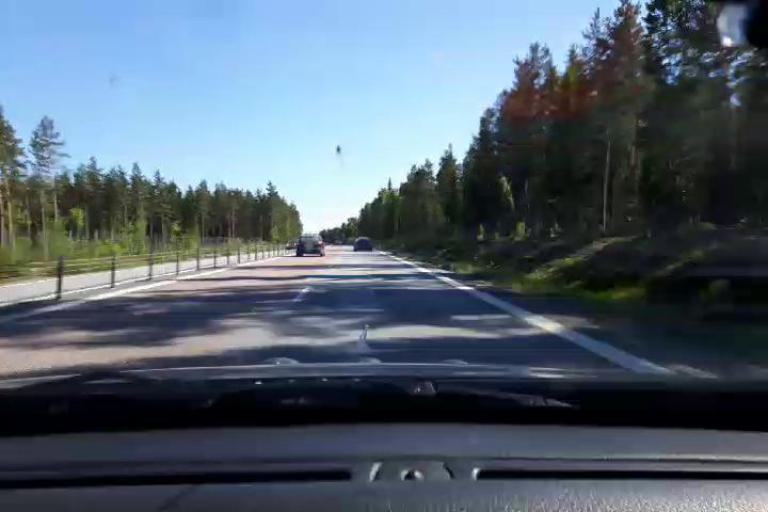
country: SE
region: Gaevleborg
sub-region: Gavle Kommun
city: Norrsundet
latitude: 60.8789
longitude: 17.0464
